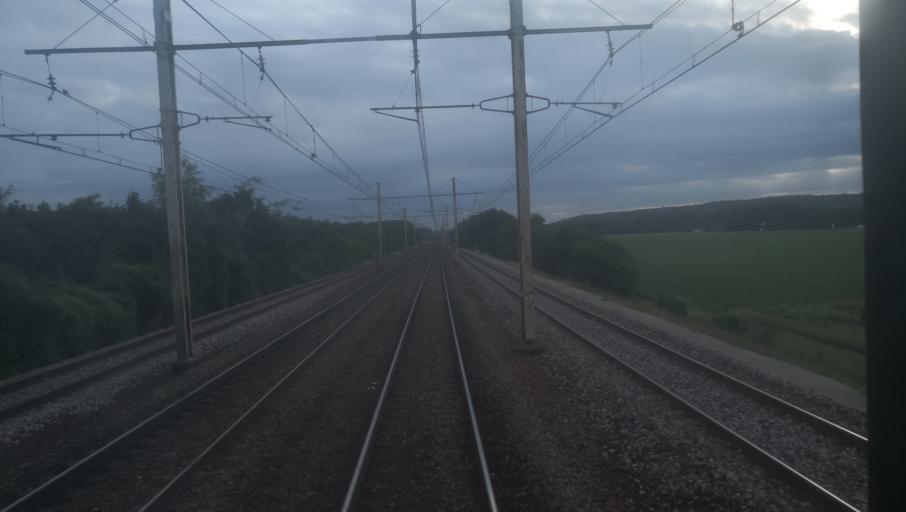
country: FR
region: Ile-de-France
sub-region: Departement de l'Essonne
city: Morigny-Champigny
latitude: 48.4599
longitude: 2.1720
